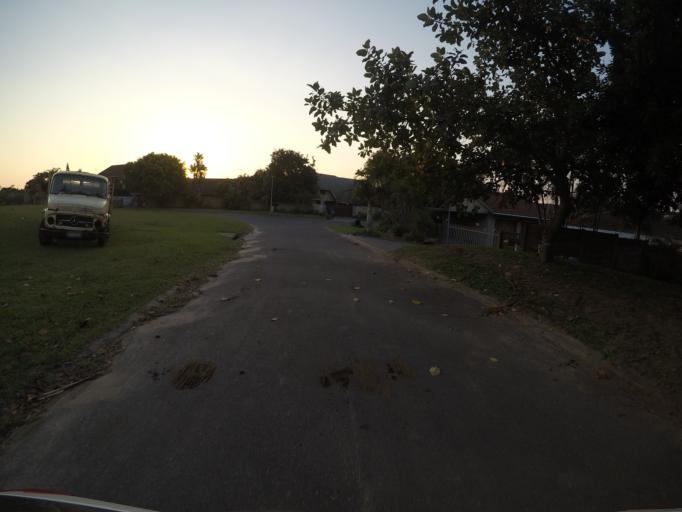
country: ZA
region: KwaZulu-Natal
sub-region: uThungulu District Municipality
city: Richards Bay
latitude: -28.7686
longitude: 32.1245
